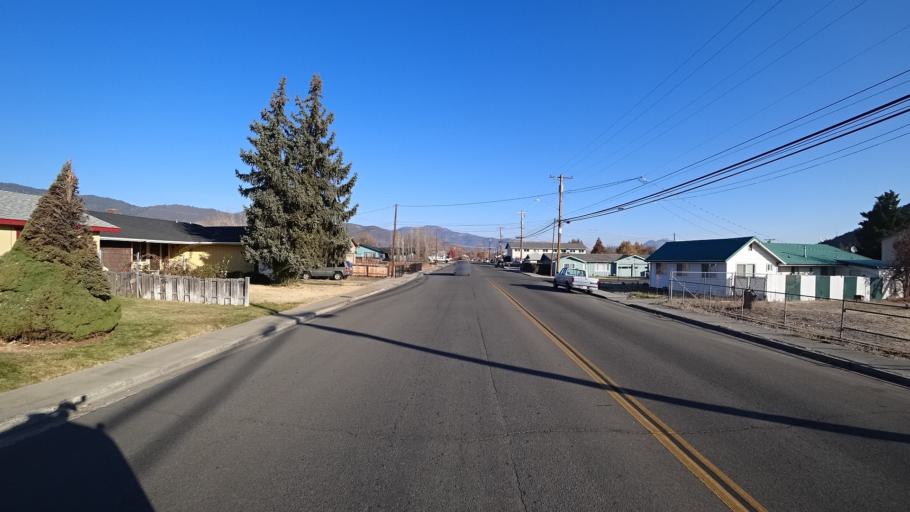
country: US
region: California
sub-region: Siskiyou County
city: Yreka
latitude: 41.7219
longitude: -122.6418
